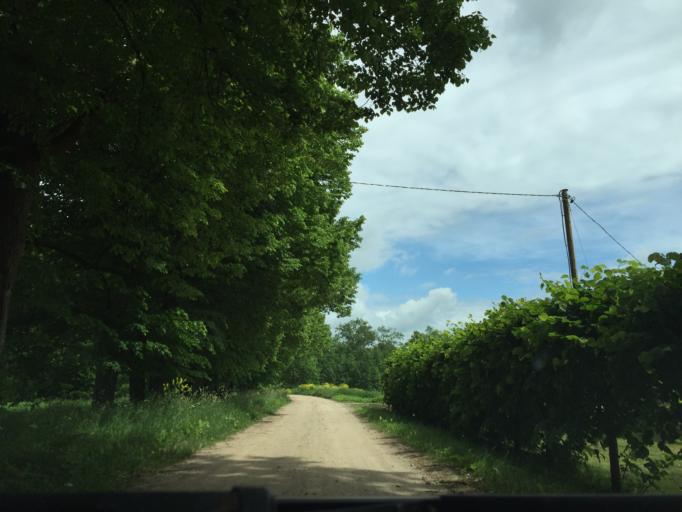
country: LV
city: Tireli
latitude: 56.6847
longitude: 23.5047
